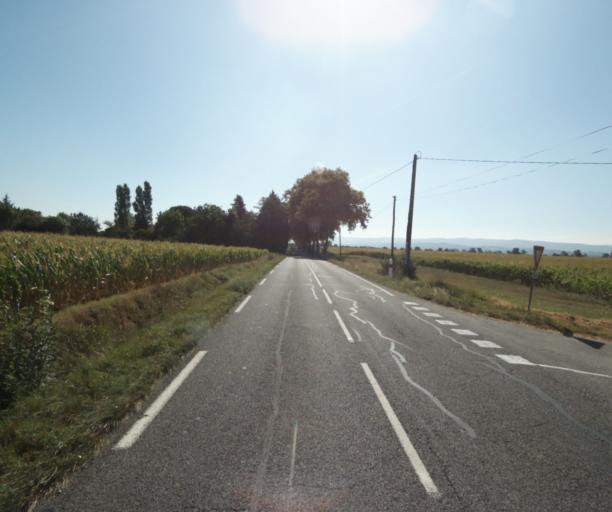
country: FR
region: Midi-Pyrenees
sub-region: Departement de la Haute-Garonne
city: Saint-Felix-Lauragais
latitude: 43.4736
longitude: 1.9401
